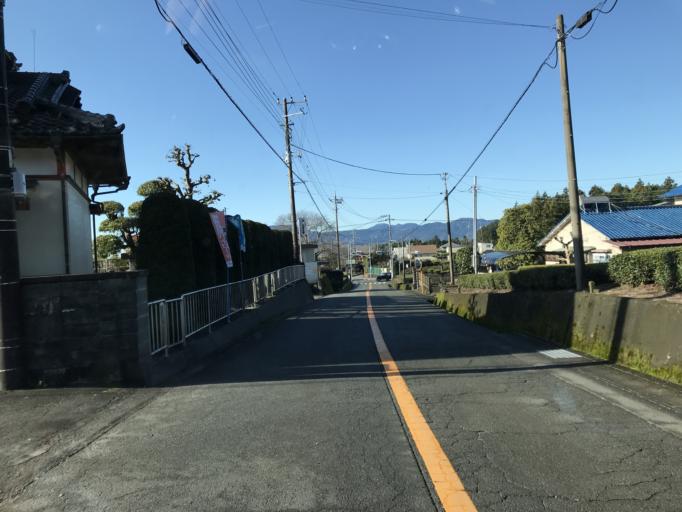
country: JP
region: Shizuoka
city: Fujinomiya
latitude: 35.2278
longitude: 138.6490
